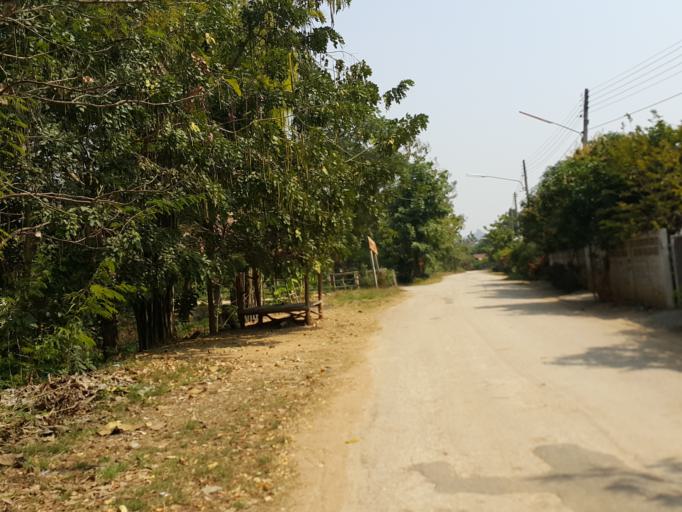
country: TH
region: Sukhothai
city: Thung Saliam
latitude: 17.3321
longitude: 99.4827
